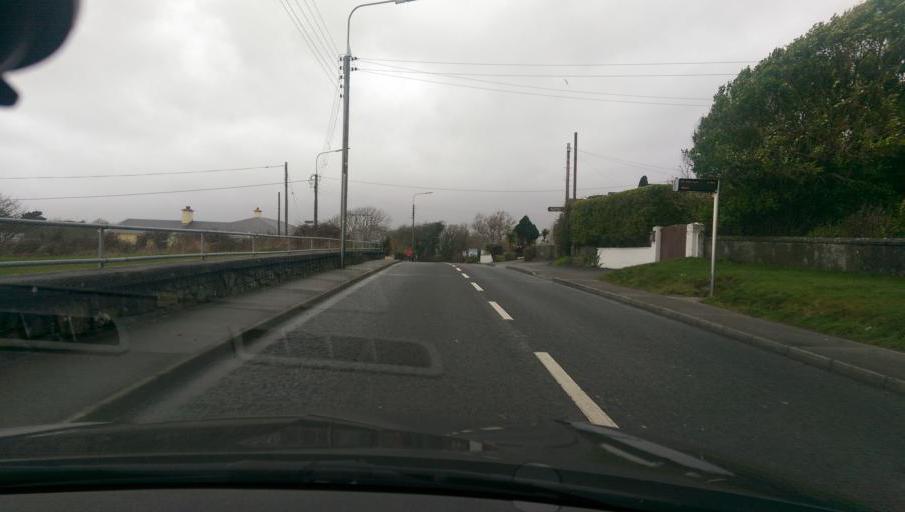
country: IE
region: Connaught
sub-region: County Galway
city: Bearna
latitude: 53.2586
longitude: -9.1039
